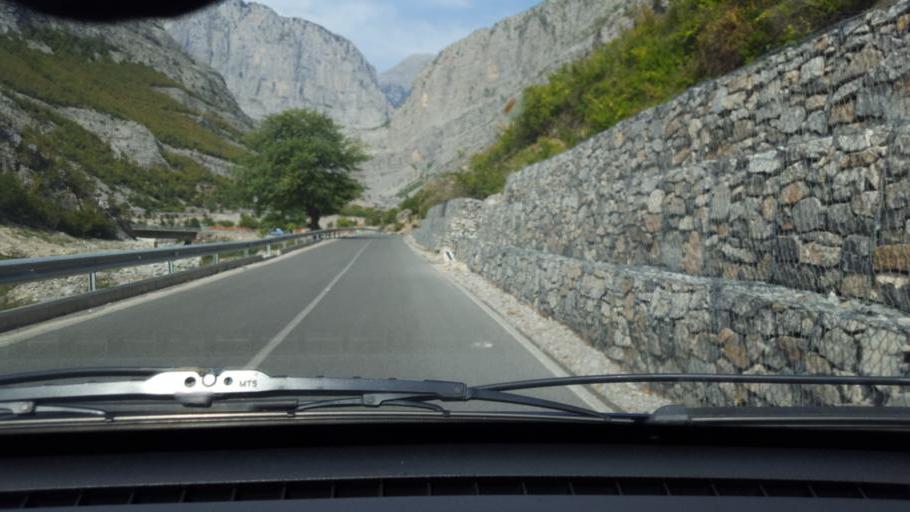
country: AL
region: Shkoder
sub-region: Rrethi i Malesia e Madhe
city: Kastrat
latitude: 42.4791
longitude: 19.5826
